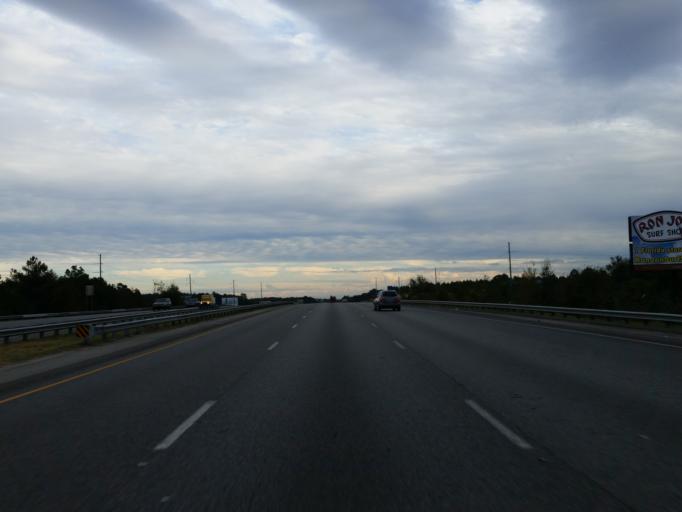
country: US
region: Georgia
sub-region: Lowndes County
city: Remerton
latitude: 30.8170
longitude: -83.3161
